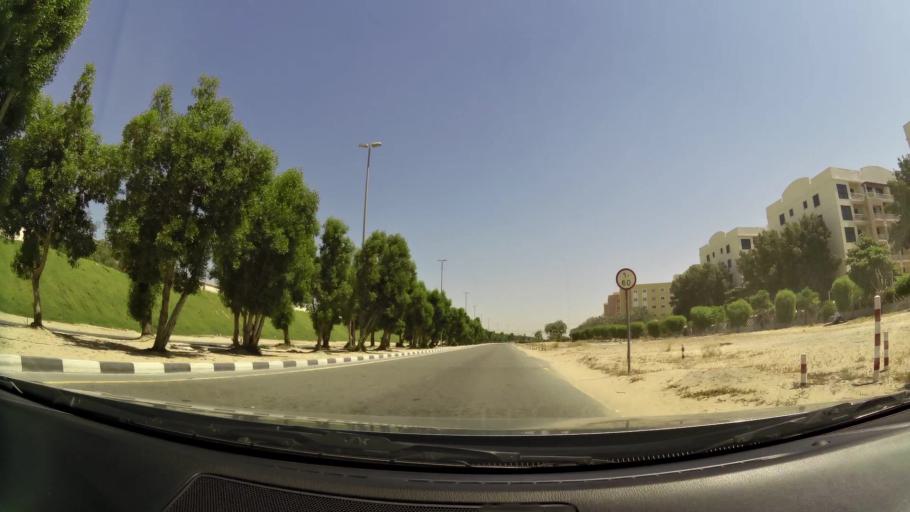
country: AE
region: Dubai
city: Dubai
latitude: 24.9853
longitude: 55.2005
